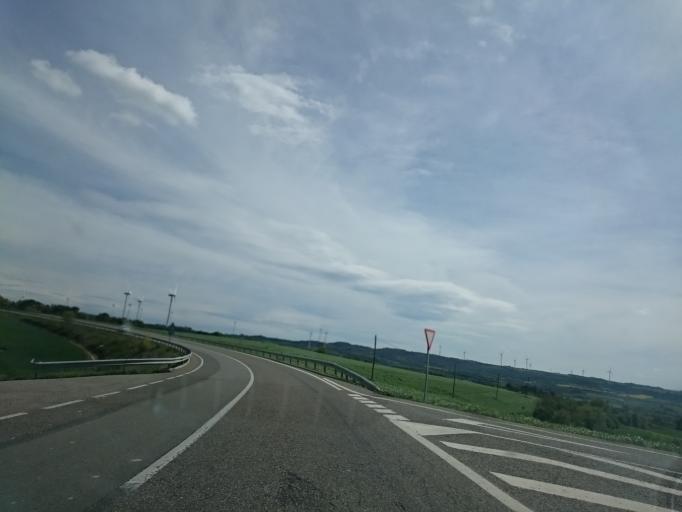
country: ES
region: Catalonia
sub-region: Provincia de Tarragona
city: Santa Coloma de Queralt
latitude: 41.5854
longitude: 1.3900
